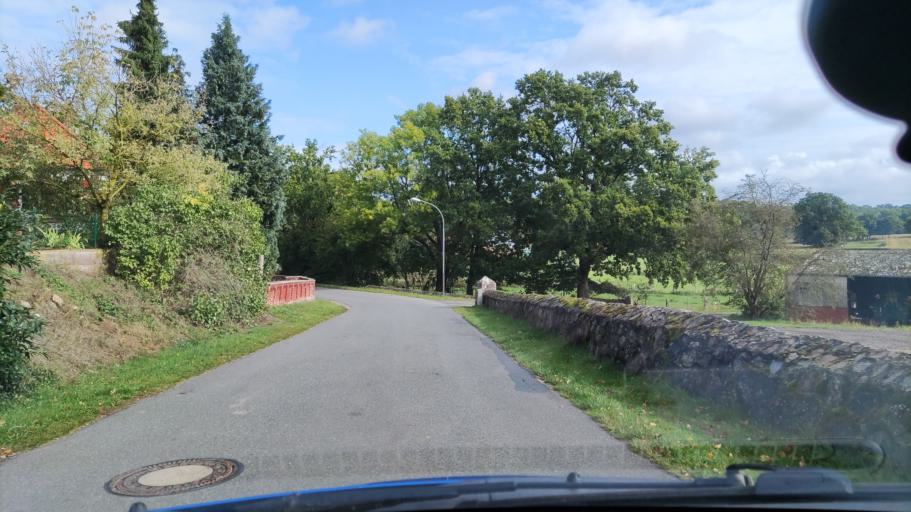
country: DE
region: Lower Saxony
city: Romstedt
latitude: 53.0812
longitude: 10.6769
